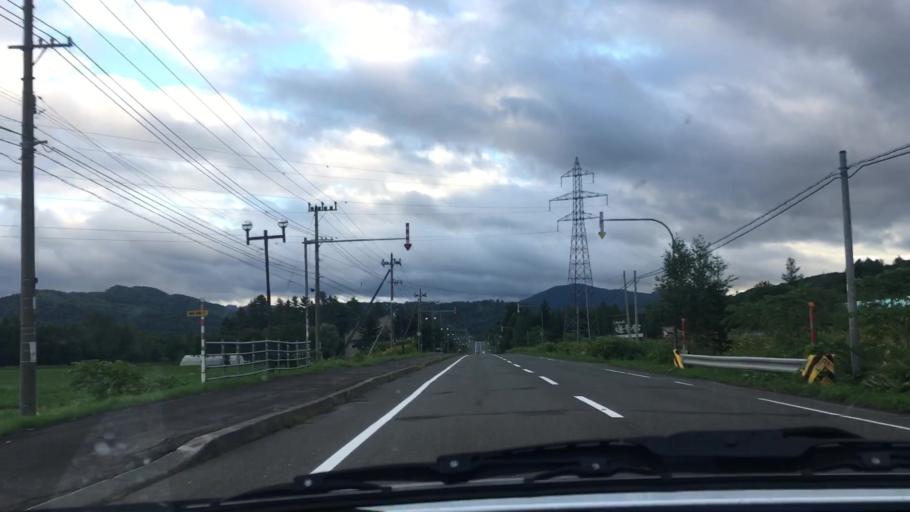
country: JP
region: Hokkaido
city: Shimo-furano
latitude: 42.9984
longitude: 142.4046
